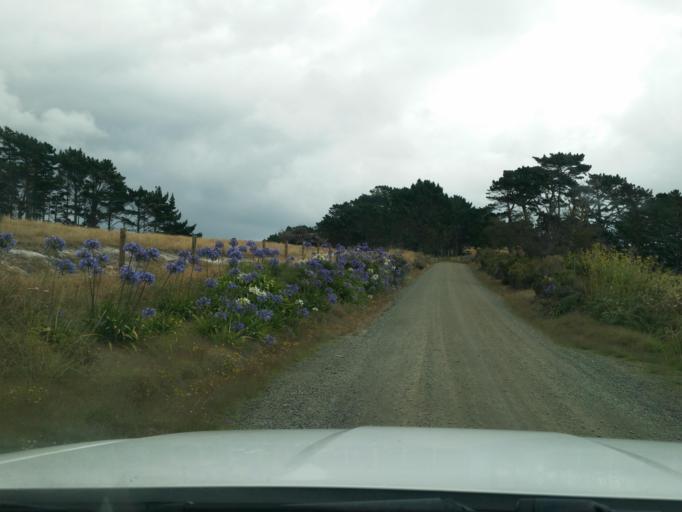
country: NZ
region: Northland
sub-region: Kaipara District
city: Dargaville
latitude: -35.9882
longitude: 173.8206
